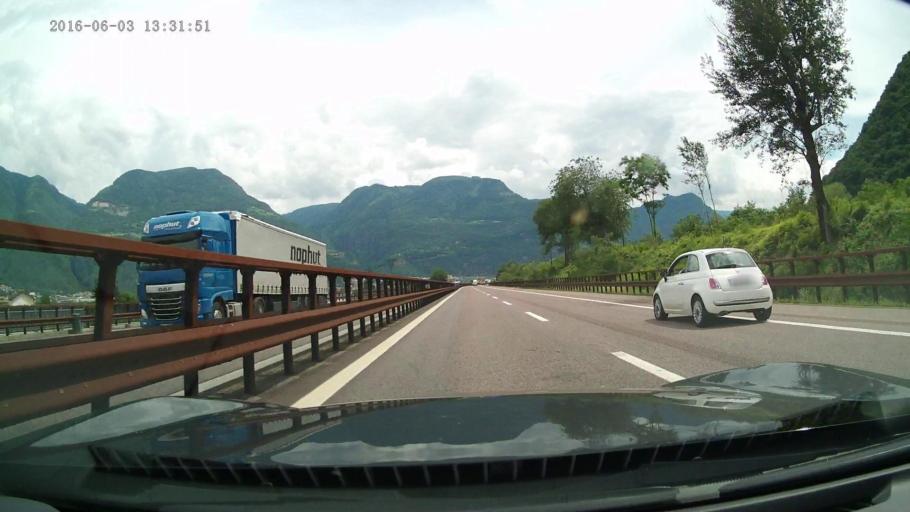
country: IT
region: Trentino-Alto Adige
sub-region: Bolzano
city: San Giacomo
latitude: 46.4451
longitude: 11.3132
